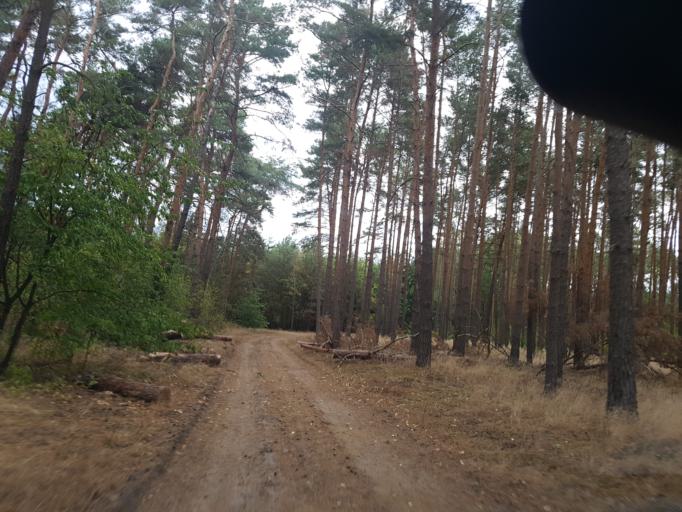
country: DE
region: Brandenburg
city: Schilda
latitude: 51.5637
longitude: 13.3283
